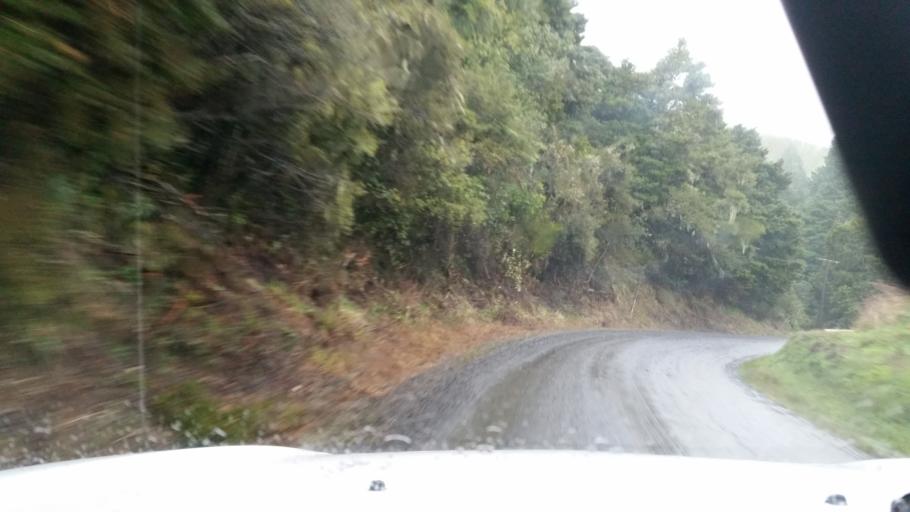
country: NZ
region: Northland
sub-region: Kaipara District
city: Dargaville
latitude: -35.7438
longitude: 173.9626
